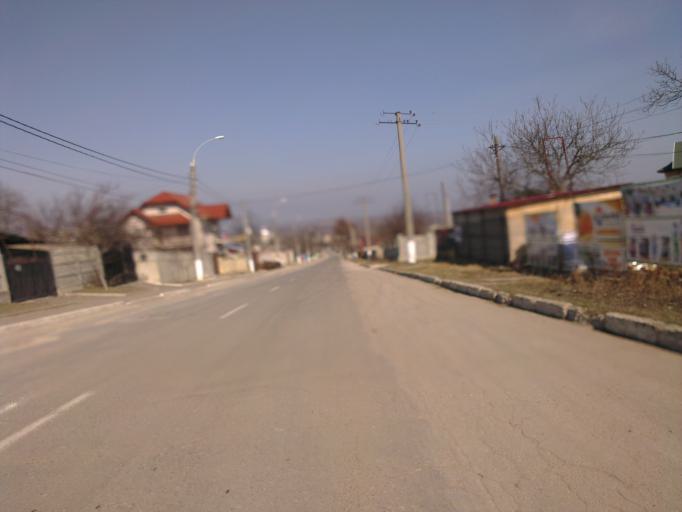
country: MD
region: Chisinau
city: Cricova
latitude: 47.1318
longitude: 28.8657
